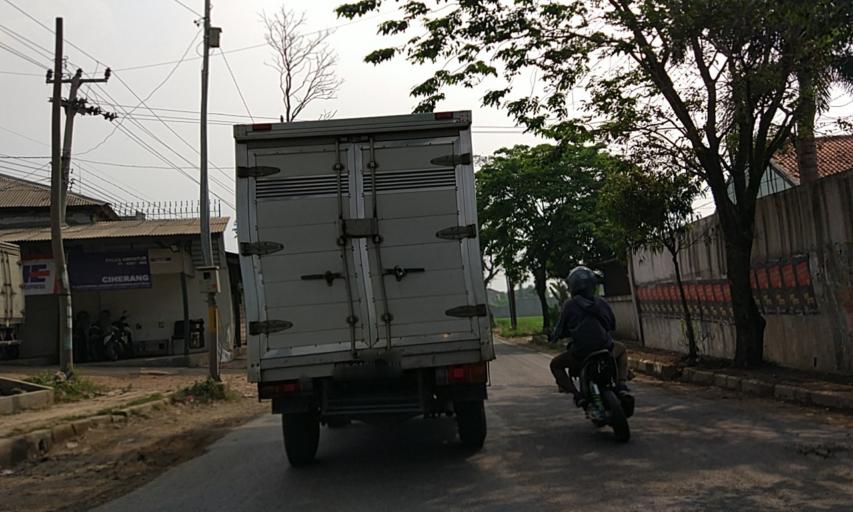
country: ID
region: West Java
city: Banjaran
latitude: -7.0455
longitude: 107.5739
